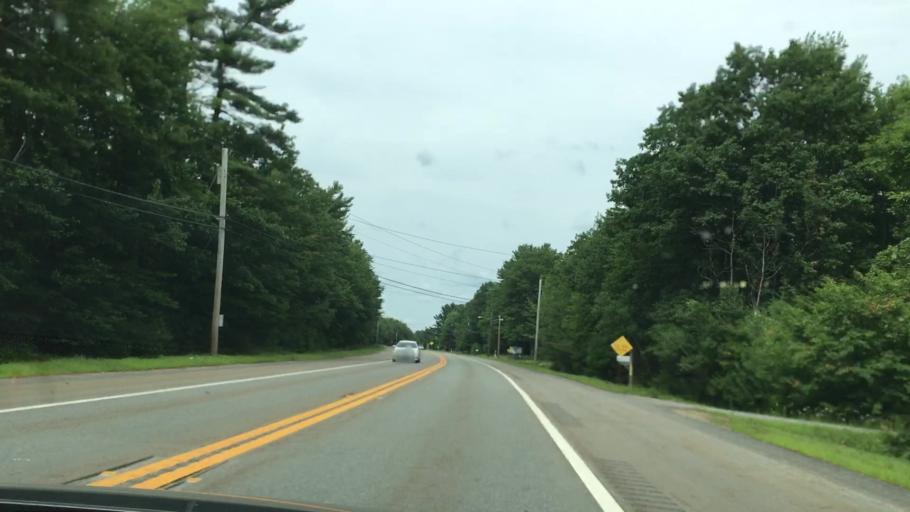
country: US
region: Massachusetts
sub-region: Worcester County
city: Gardner
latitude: 42.6297
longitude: -72.0077
